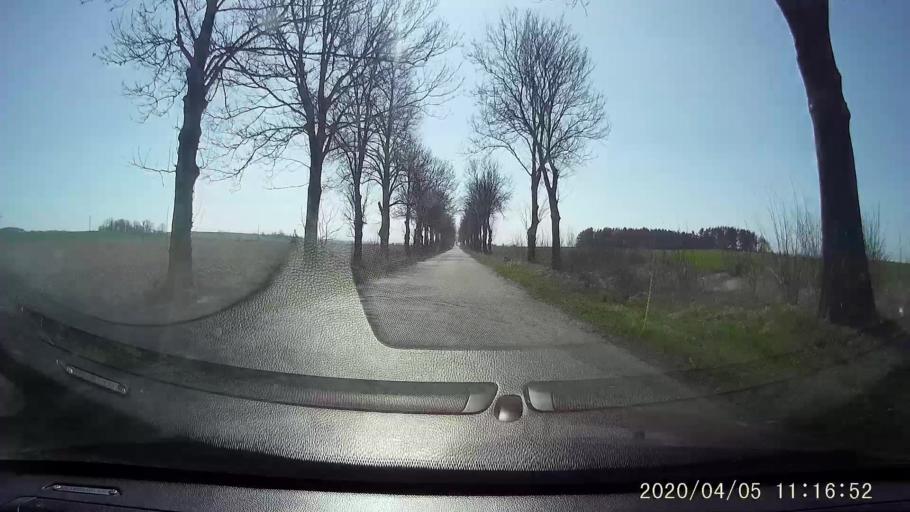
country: PL
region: Lower Silesian Voivodeship
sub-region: Powiat zgorzelecki
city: Sulikow
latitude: 51.0767
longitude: 15.1035
